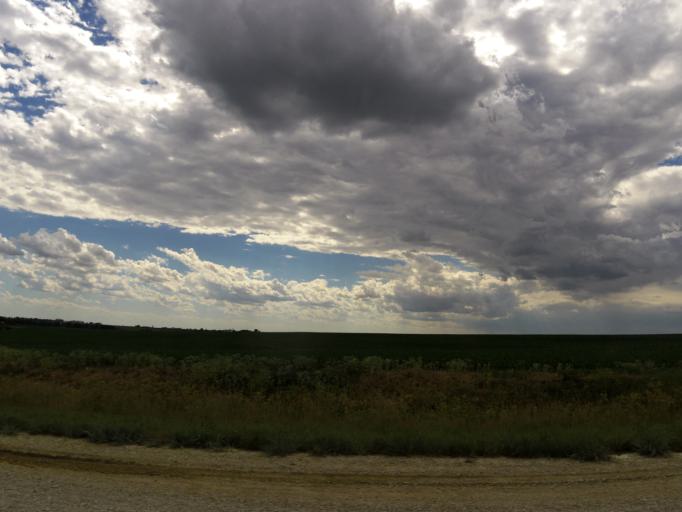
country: US
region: Iowa
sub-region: Henry County
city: Mount Pleasant
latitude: 40.8075
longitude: -91.5648
